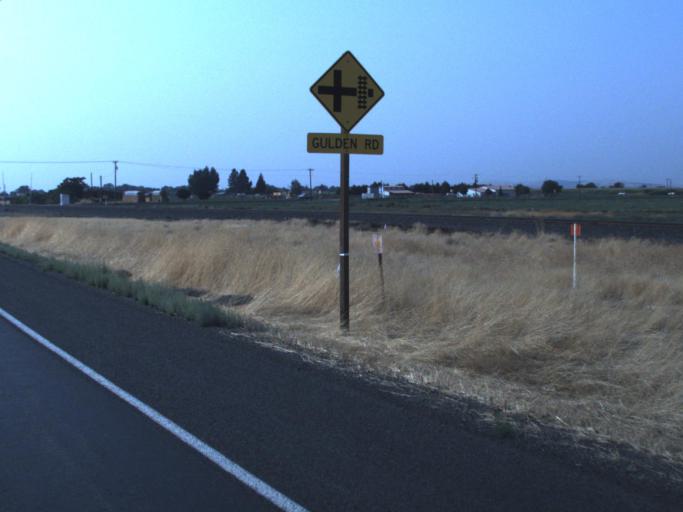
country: US
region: Washington
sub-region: Yakima County
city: Mabton
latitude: 46.2066
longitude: -119.9788
